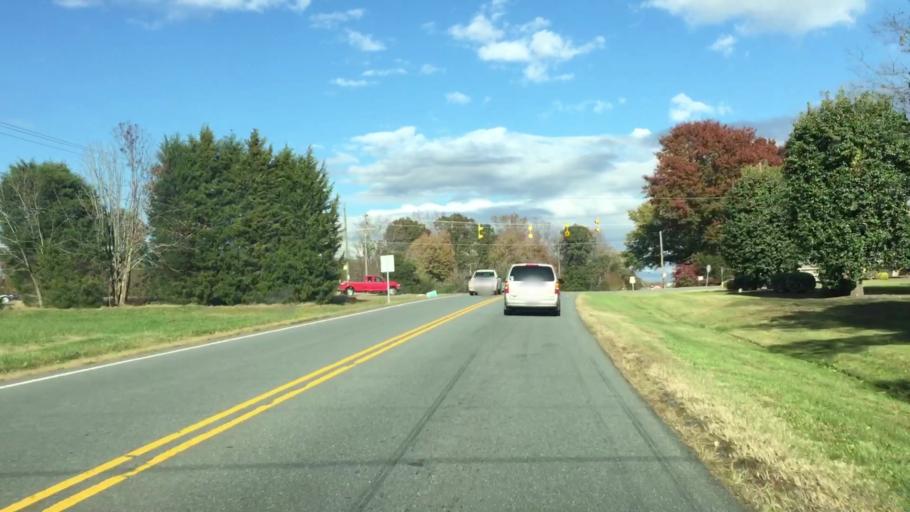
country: US
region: North Carolina
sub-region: Guilford County
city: Oak Ridge
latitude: 36.2122
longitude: -80.0666
